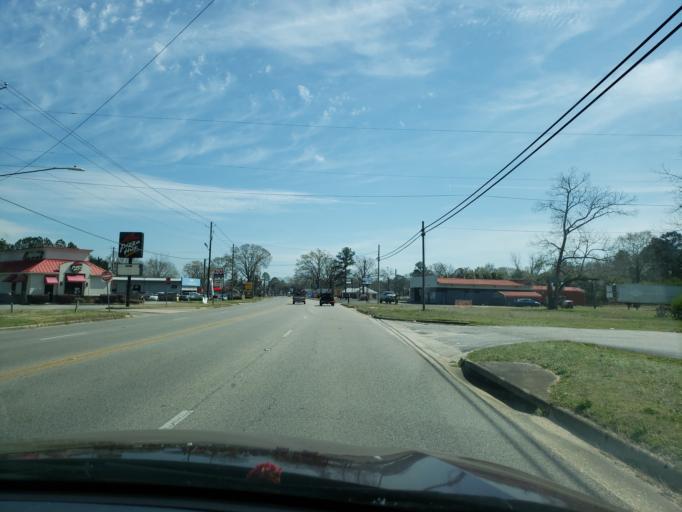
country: US
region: Alabama
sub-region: Elmore County
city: Tallassee
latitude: 32.5546
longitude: -85.9241
